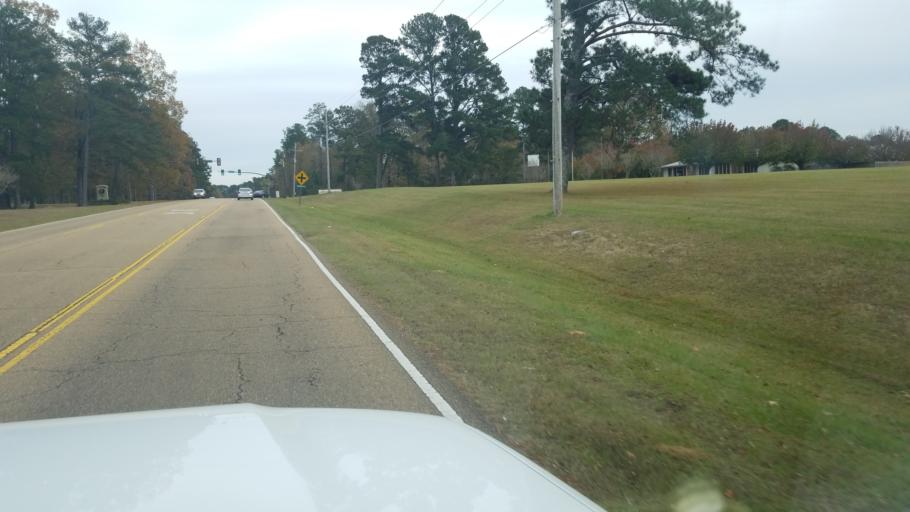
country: US
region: Mississippi
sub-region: Rankin County
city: Brandon
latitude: 32.3755
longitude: -90.0244
